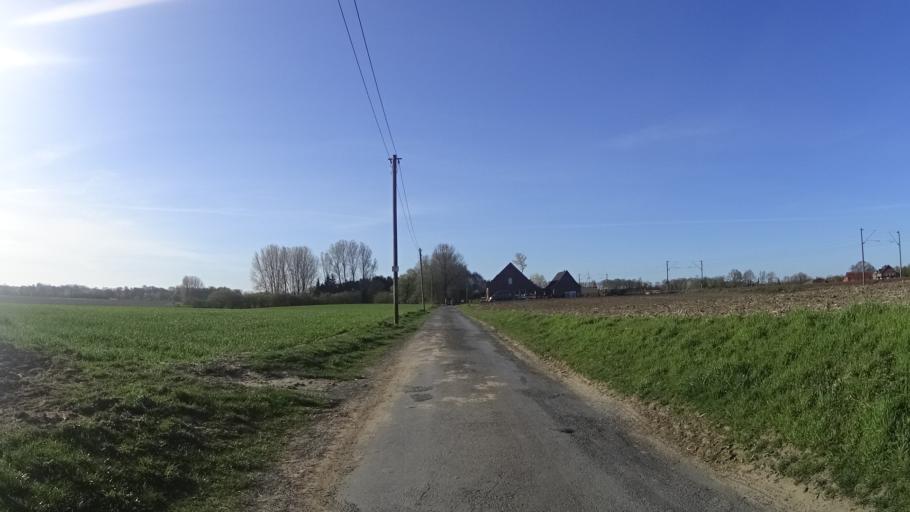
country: DE
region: North Rhine-Westphalia
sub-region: Regierungsbezirk Munster
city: Greven
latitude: 52.0806
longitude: 7.6042
